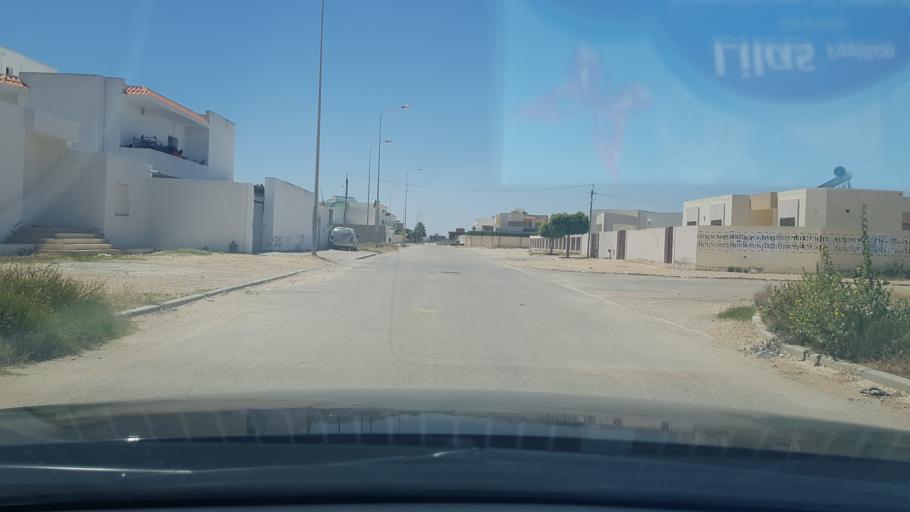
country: TN
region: Safaqis
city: Al Qarmadah
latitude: 34.8362
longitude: 10.7602
